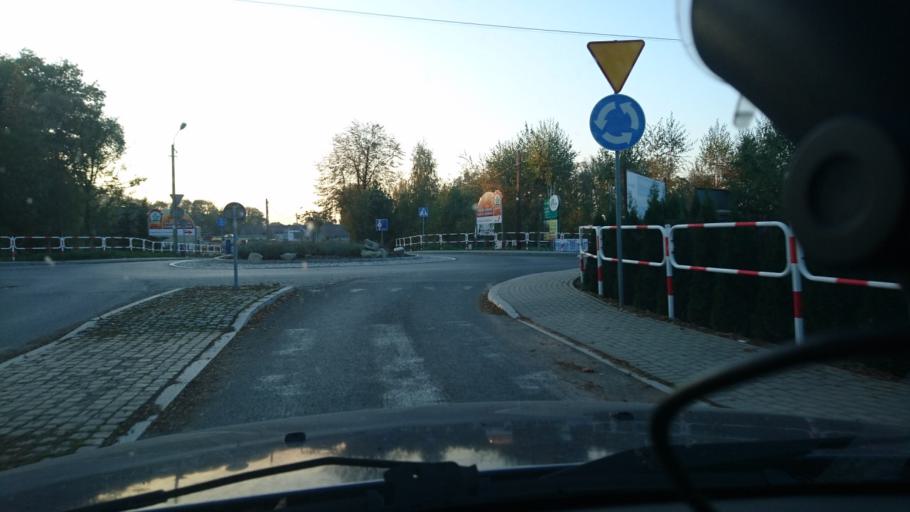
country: PL
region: Silesian Voivodeship
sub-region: Powiat bielski
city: Pisarzowice
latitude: 49.8742
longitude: 19.1408
